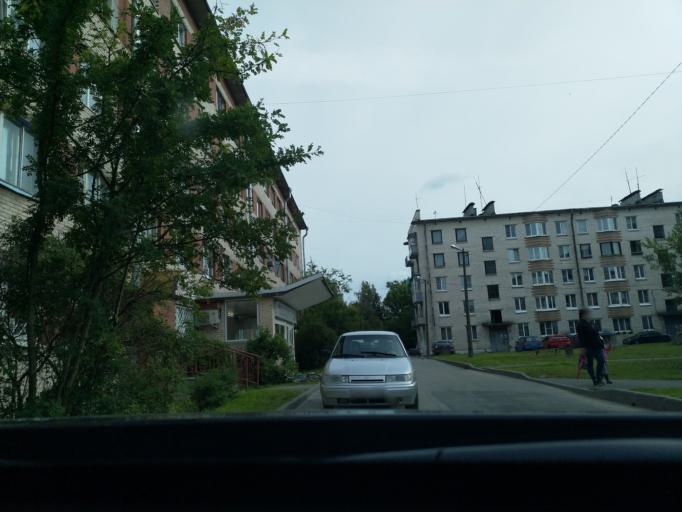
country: RU
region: Leningrad
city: Nikol'skoye
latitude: 59.7040
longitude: 30.7901
